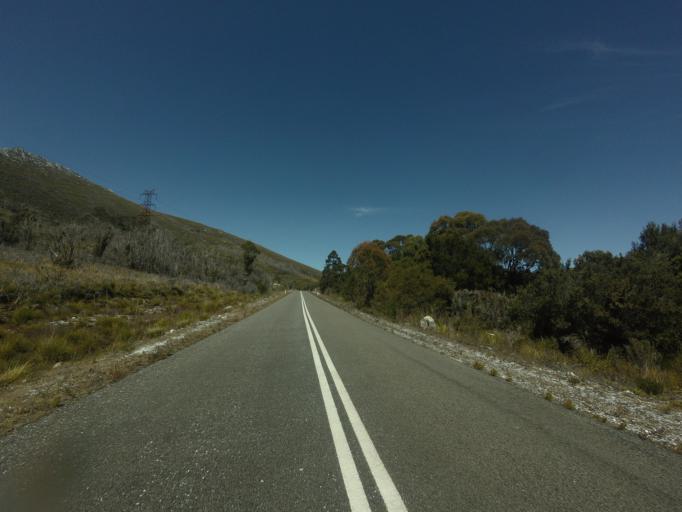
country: AU
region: Tasmania
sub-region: Huon Valley
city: Geeveston
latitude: -42.8400
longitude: 146.1600
